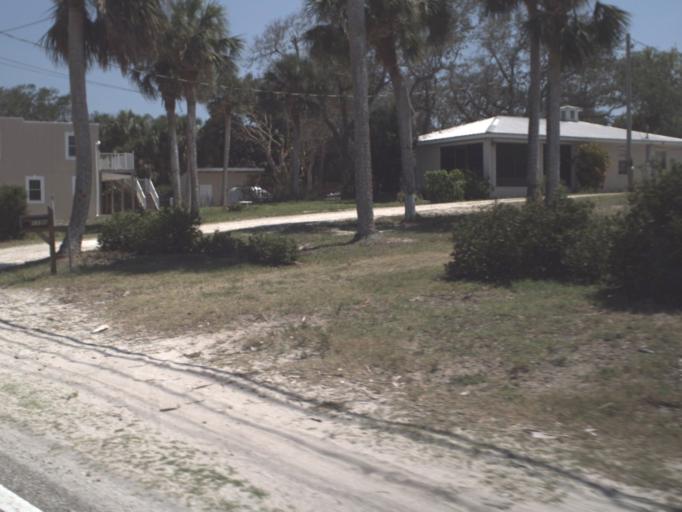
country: US
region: Florida
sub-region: Brevard County
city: Malabar
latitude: 28.0073
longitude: -80.5657
